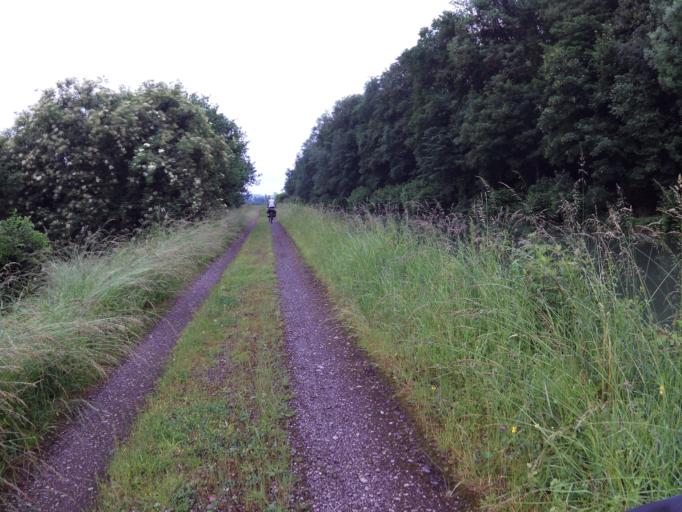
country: FR
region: Lorraine
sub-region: Departement de la Meuse
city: Fains-Veel
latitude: 48.8033
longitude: 5.1060
